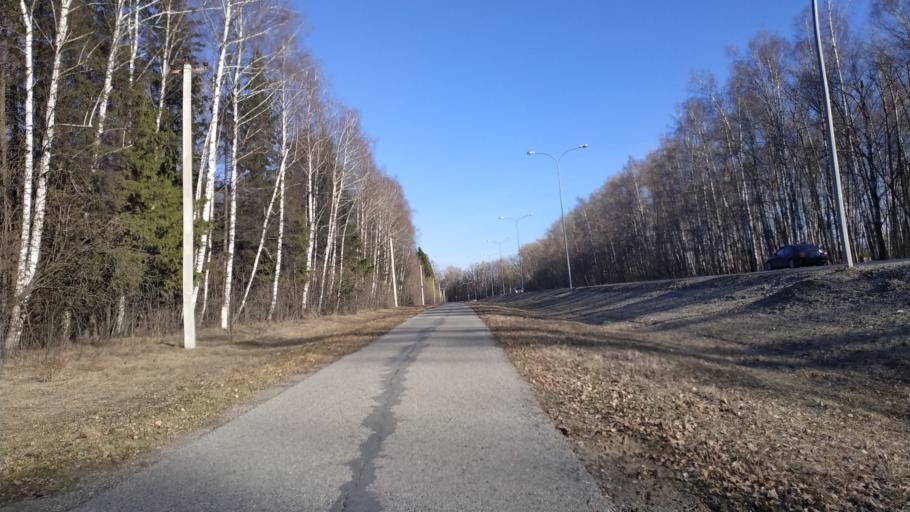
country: RU
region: Chuvashia
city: Novyye Lapsary
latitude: 56.1302
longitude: 47.1156
